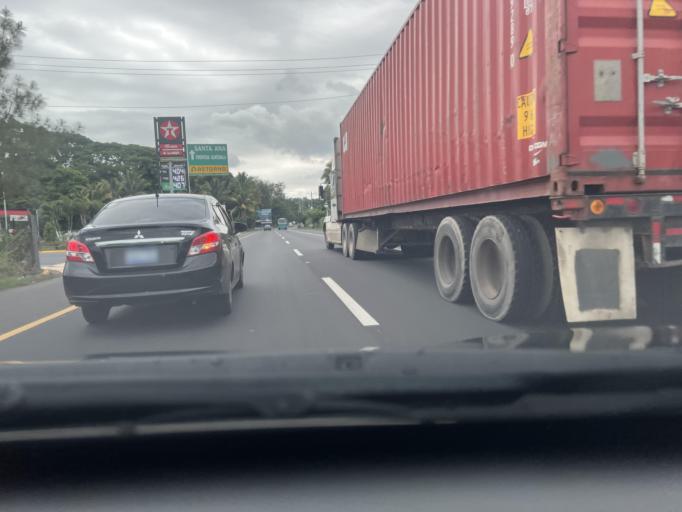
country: SV
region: Santa Ana
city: El Congo
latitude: 13.8837
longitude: -89.4947
